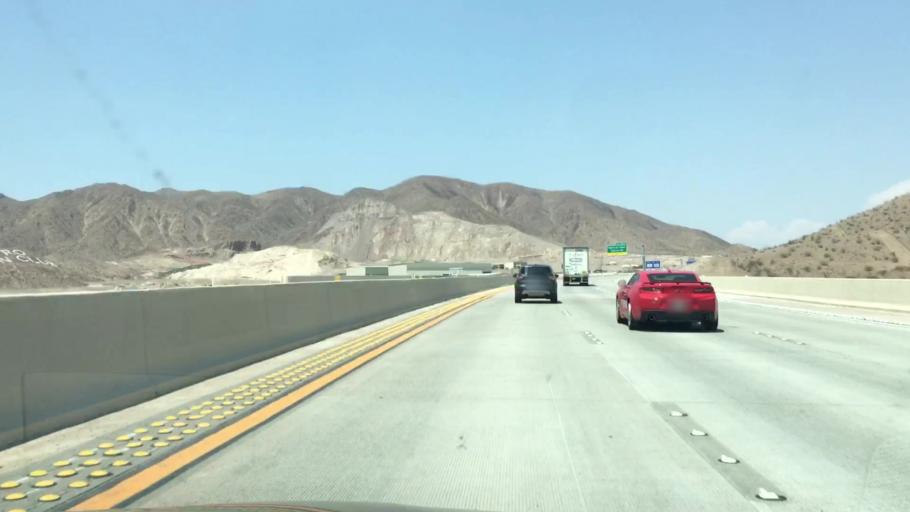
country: US
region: Nevada
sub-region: Clark County
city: Boulder City
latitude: 35.9568
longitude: -114.9085
